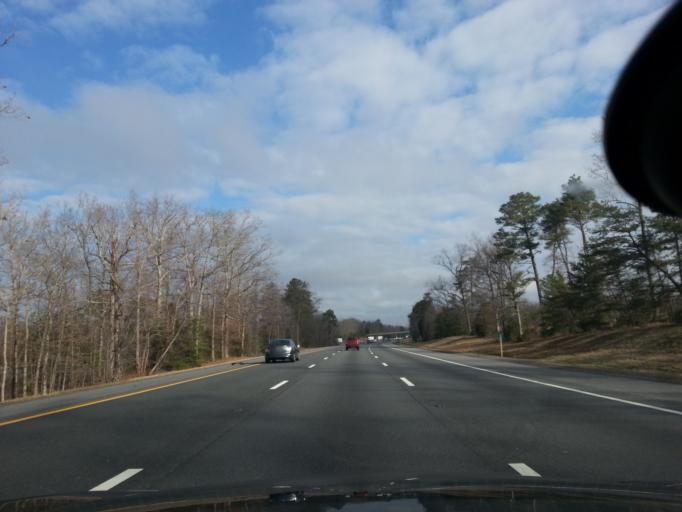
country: US
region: Virginia
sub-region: Spotsylvania County
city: Spotsylvania Courthouse
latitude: 38.0844
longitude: -77.5159
